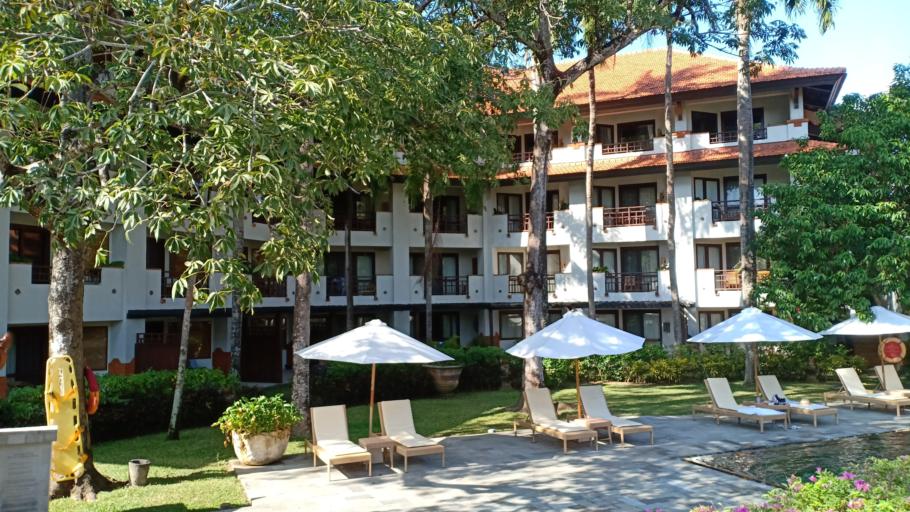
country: ID
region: Bali
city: Bualu
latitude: -8.8024
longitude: 115.2332
